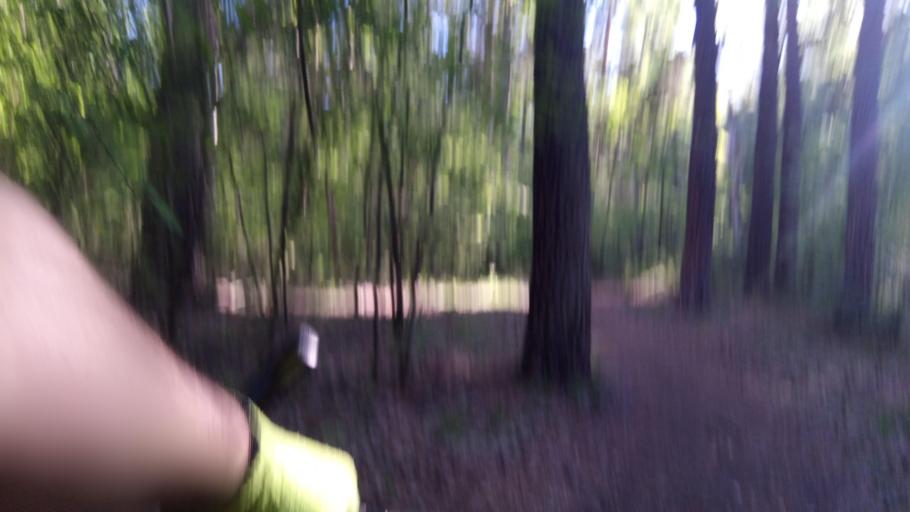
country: RU
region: Chelyabinsk
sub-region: Gorod Chelyabinsk
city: Chelyabinsk
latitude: 55.1433
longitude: 61.3409
